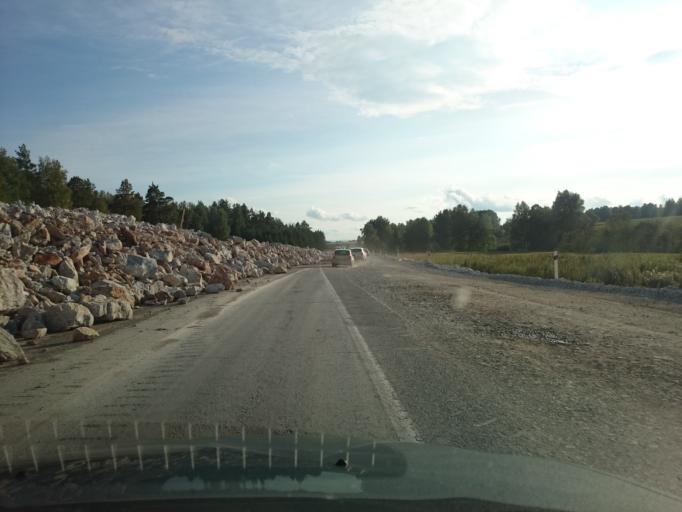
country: RU
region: Bashkortostan
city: Lomovka
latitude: 53.9099
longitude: 58.1764
